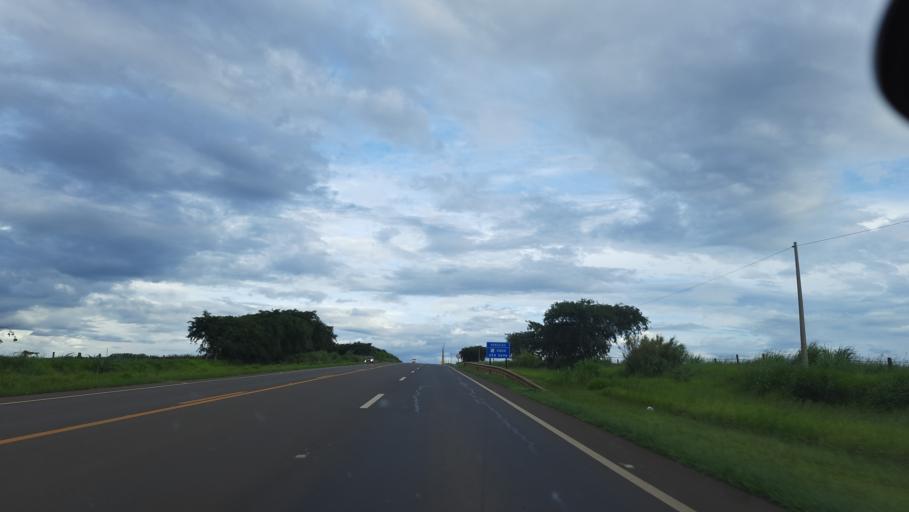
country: BR
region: Sao Paulo
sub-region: Vargem Grande Do Sul
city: Vargem Grande do Sul
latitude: -21.8118
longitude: -46.9911
